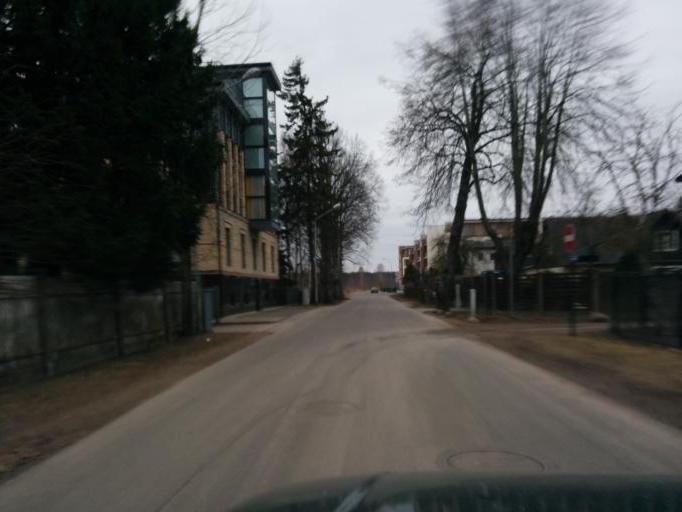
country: LV
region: Jurmala
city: Jurmala
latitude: 56.9631
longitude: 23.8189
